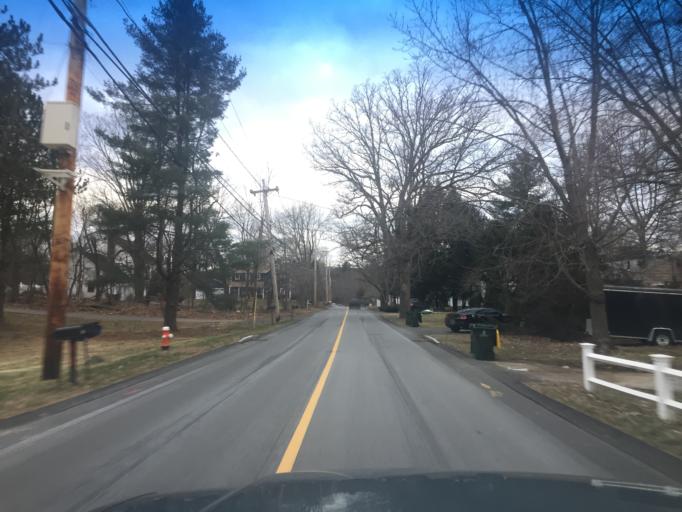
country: US
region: Massachusetts
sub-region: Norfolk County
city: Medway
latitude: 42.1267
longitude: -71.4055
